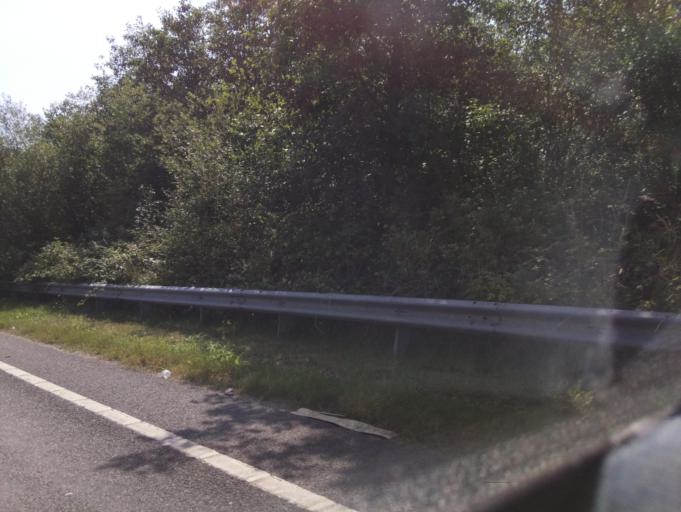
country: GB
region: Wales
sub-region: Caerphilly County Borough
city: Bargoed
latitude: 51.6814
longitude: -3.2225
